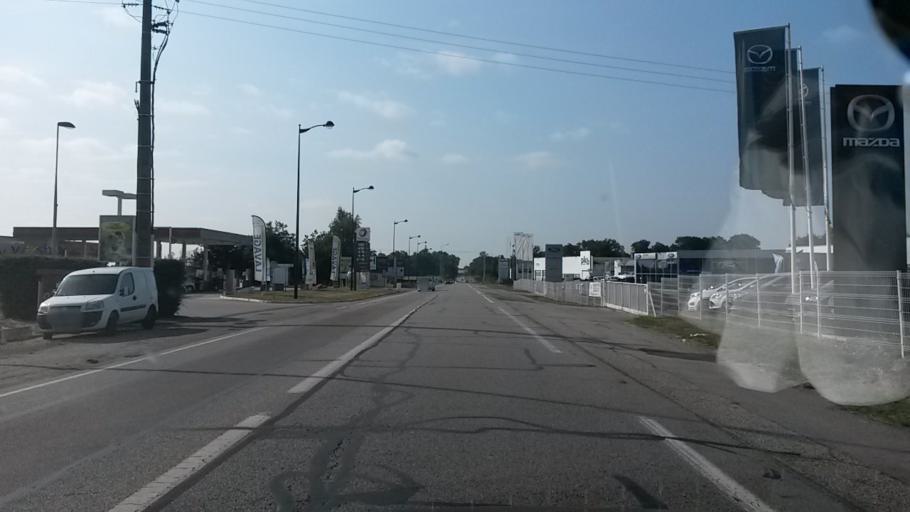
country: FR
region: Haute-Normandie
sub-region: Departement de l'Eure
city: Evreux
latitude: 48.9964
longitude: 1.1554
